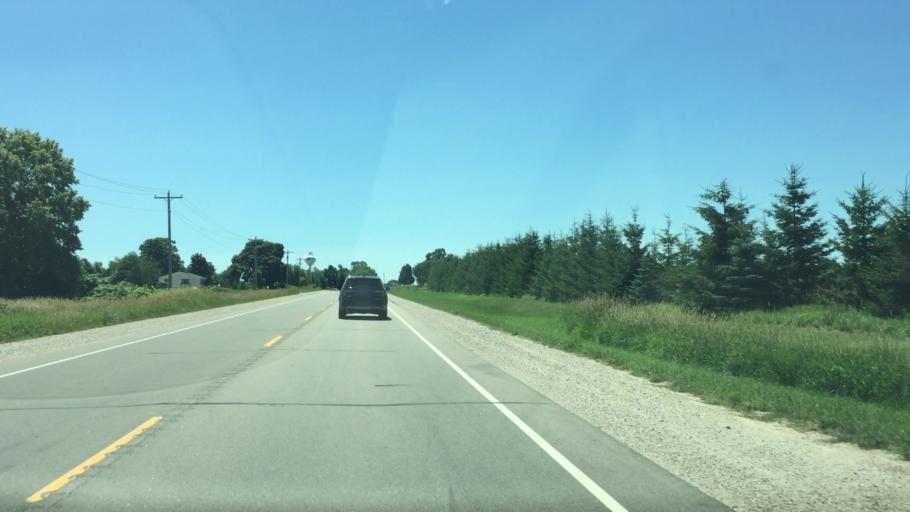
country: US
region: Wisconsin
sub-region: Calumet County
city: New Holstein
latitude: 43.9666
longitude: -88.1124
